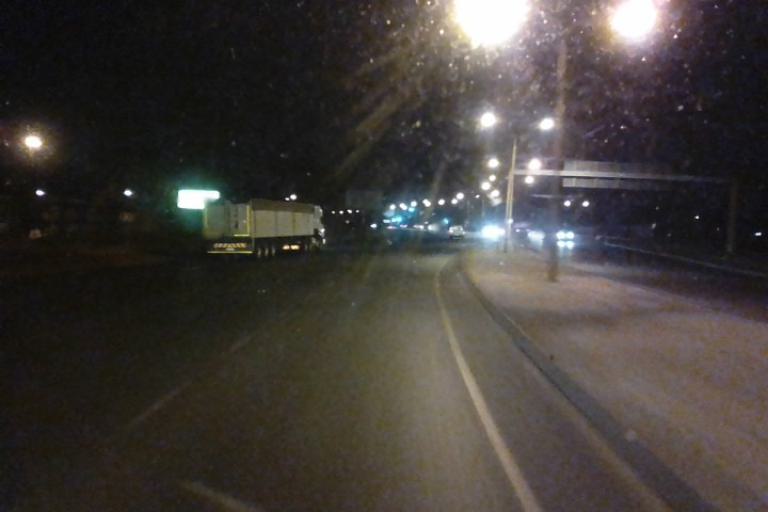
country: ZA
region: Gauteng
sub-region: Ekurhuleni Metropolitan Municipality
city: Germiston
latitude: -26.2789
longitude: 28.1235
